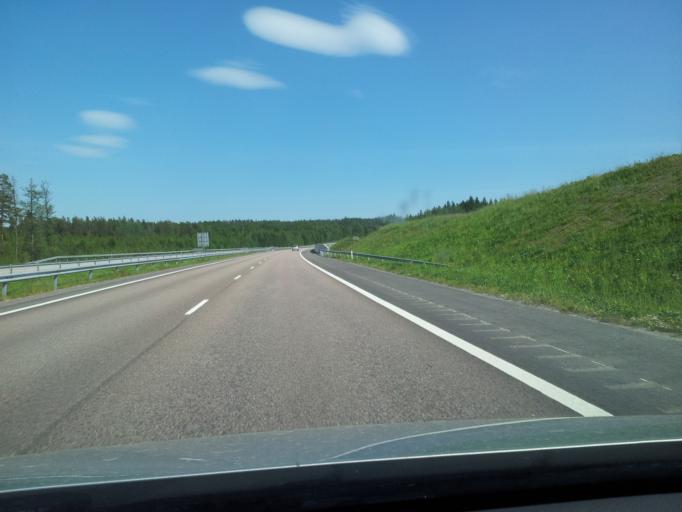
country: FI
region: Uusimaa
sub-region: Loviisa
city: Perna
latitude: 60.4903
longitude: 25.9965
